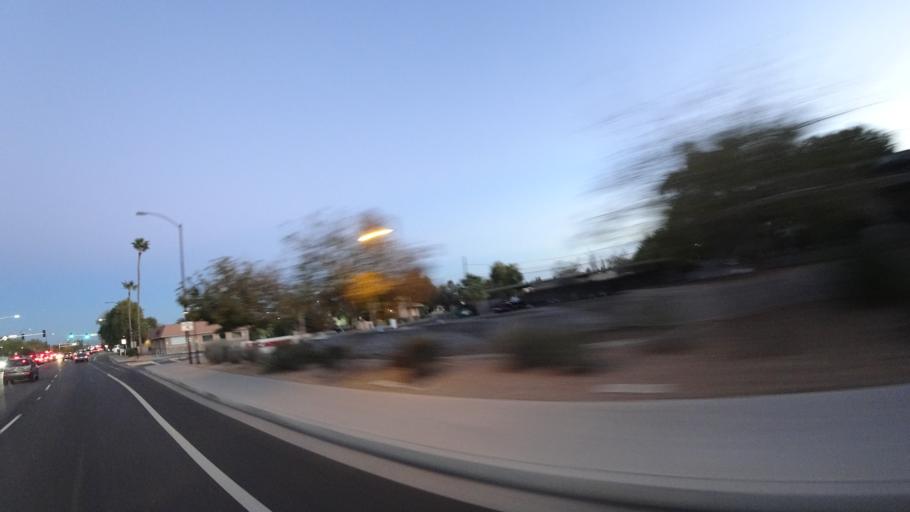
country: US
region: Arizona
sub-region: Maricopa County
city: Scottsdale
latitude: 33.4948
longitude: -111.9190
